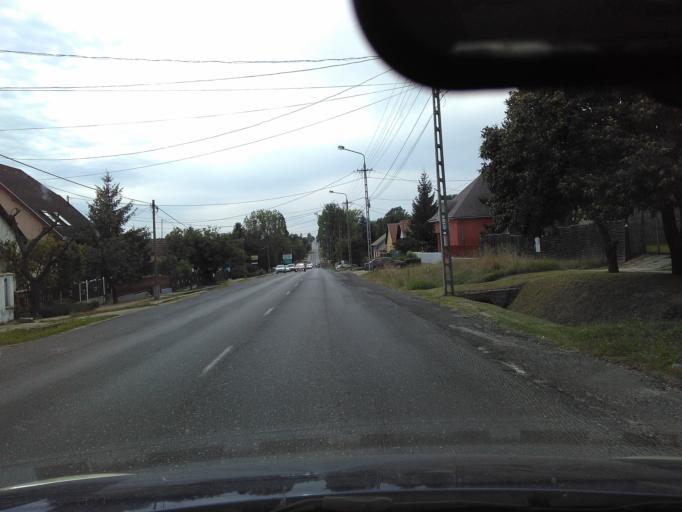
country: HU
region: Pest
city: Kerepes
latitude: 47.5569
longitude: 19.2779
